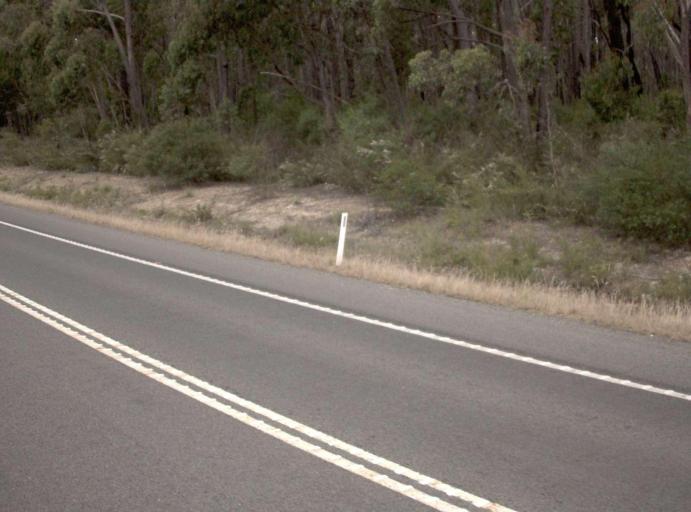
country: AU
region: Victoria
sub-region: East Gippsland
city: Lakes Entrance
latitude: -37.7283
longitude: 147.9471
